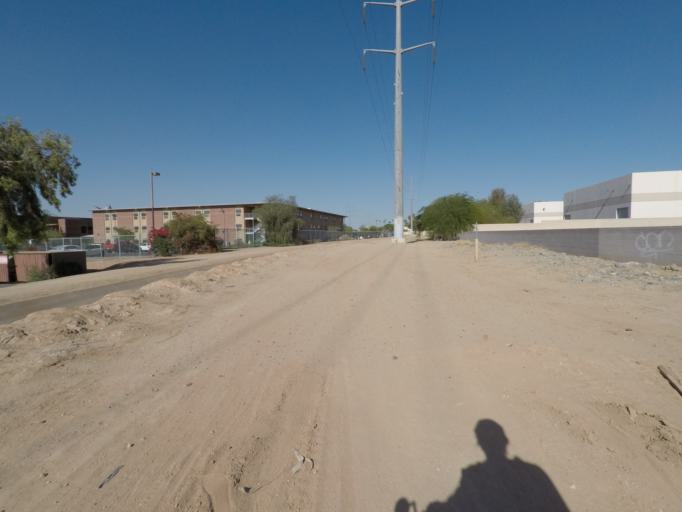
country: US
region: Arizona
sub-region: Maricopa County
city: Guadalupe
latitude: 33.3766
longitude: -111.9770
